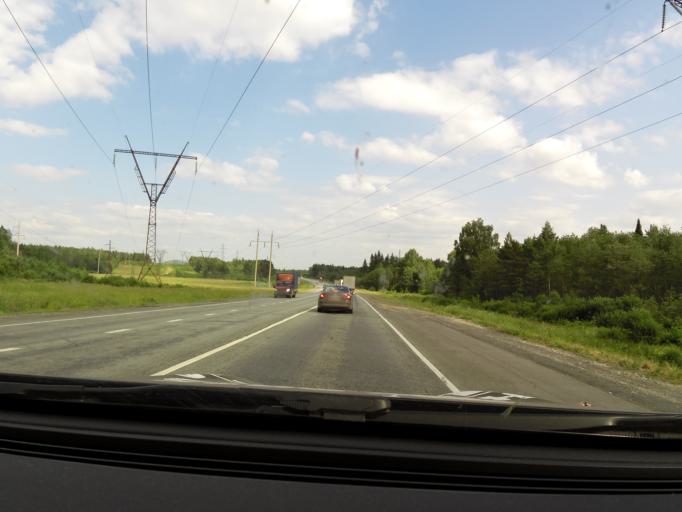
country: RU
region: Sverdlovsk
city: Revda
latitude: 56.8280
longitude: 59.8609
